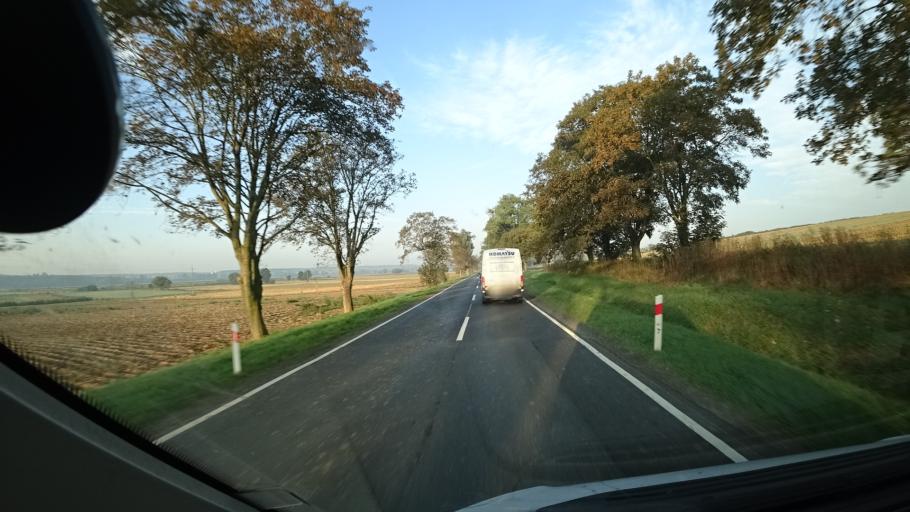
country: PL
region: Opole Voivodeship
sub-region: Powiat strzelecki
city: Ujazd
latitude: 50.3873
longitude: 18.3791
